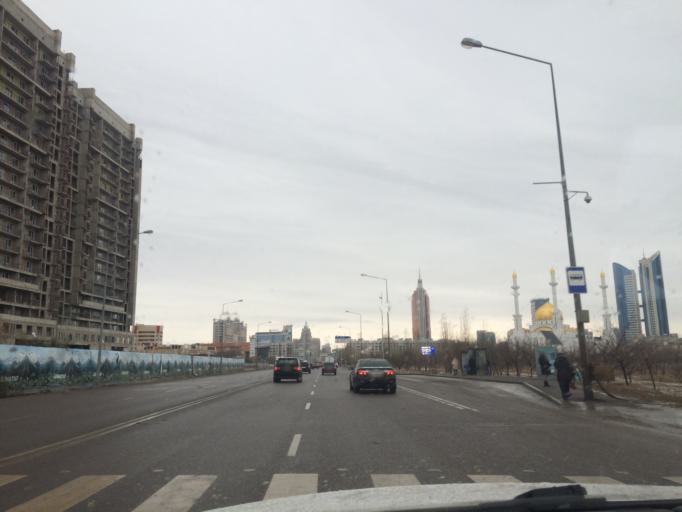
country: KZ
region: Astana Qalasy
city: Astana
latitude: 51.1231
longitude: 71.4127
